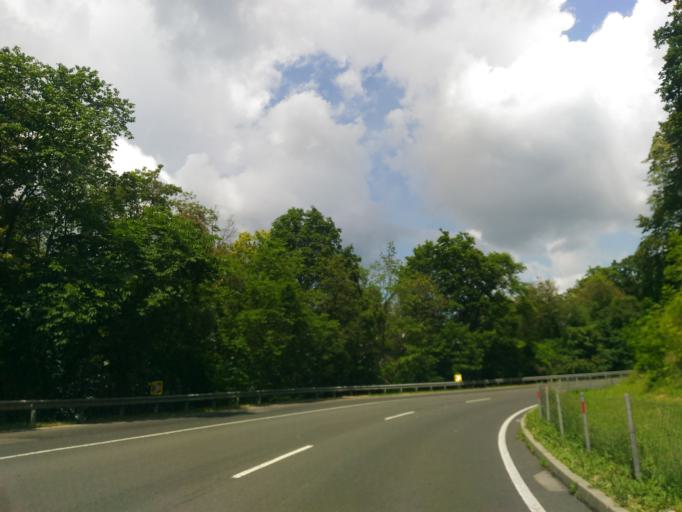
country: HU
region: Baranya
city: Komlo
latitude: 46.1472
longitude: 18.2450
